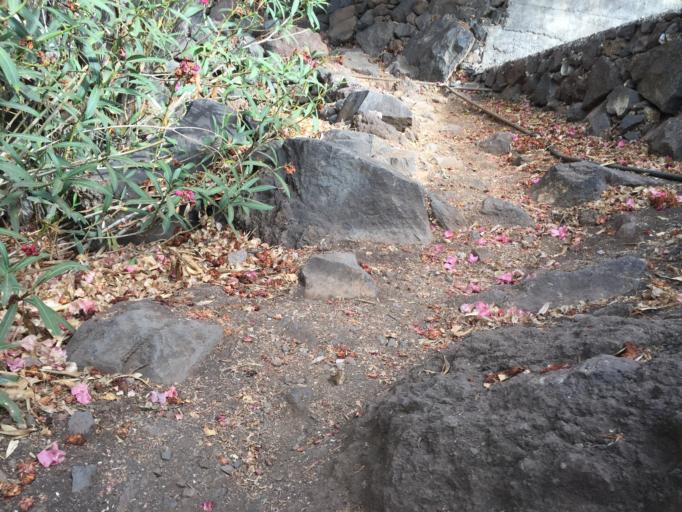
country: ES
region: Canary Islands
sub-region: Provincia de Santa Cruz de Tenerife
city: Tijarafe
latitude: 28.7217
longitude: -17.9793
